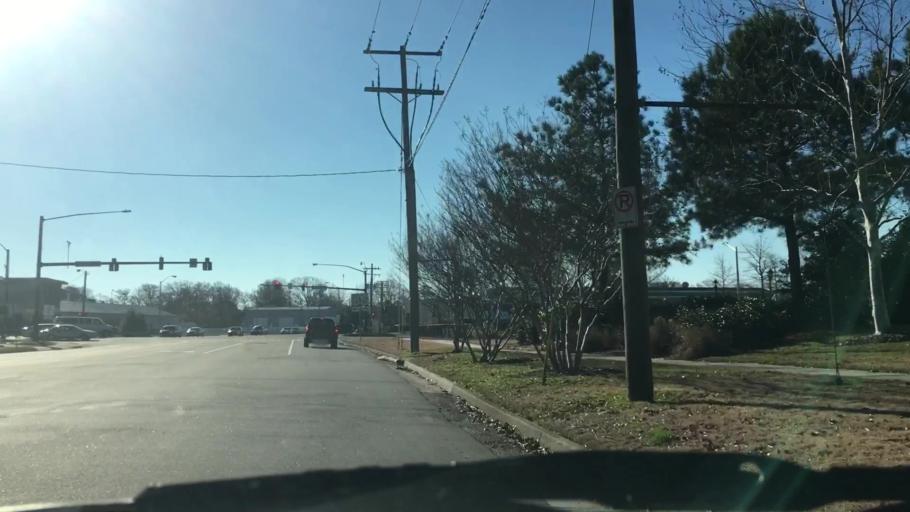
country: US
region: Virginia
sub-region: City of Norfolk
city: Norfolk
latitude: 36.8539
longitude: -76.2484
